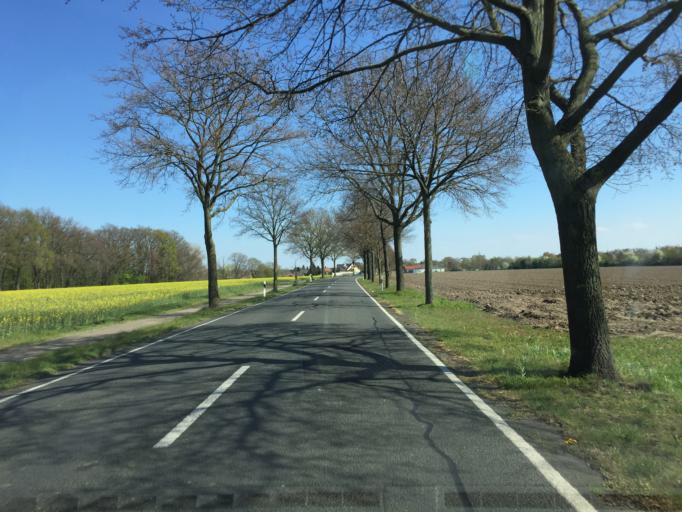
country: DE
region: Lower Saxony
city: Garbsen
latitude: 52.4038
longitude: 9.5443
